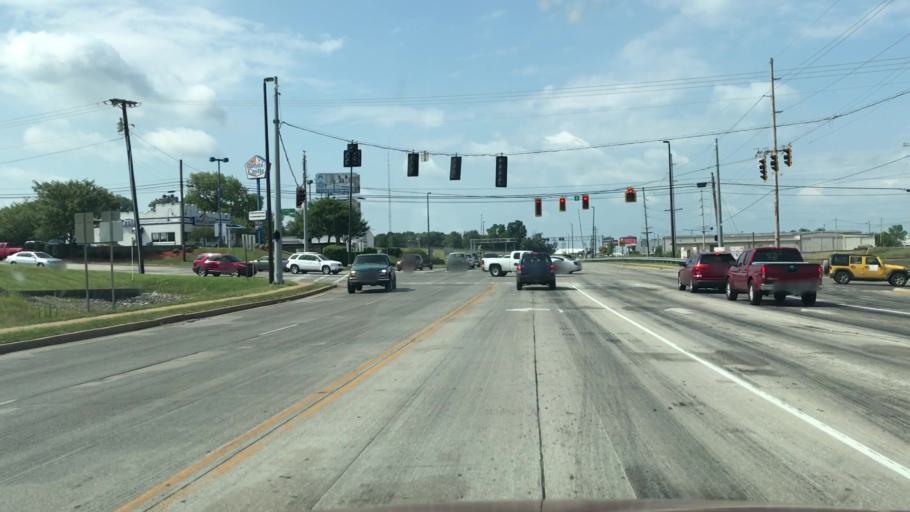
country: US
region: Kentucky
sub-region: Barren County
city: Glasgow
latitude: 37.0026
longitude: -85.9262
